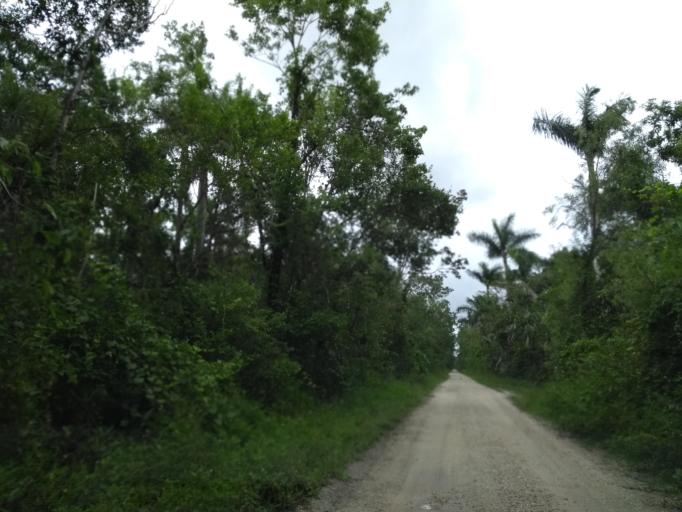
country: US
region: Florida
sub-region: Collier County
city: Lely Resort
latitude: 26.0010
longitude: -81.4111
